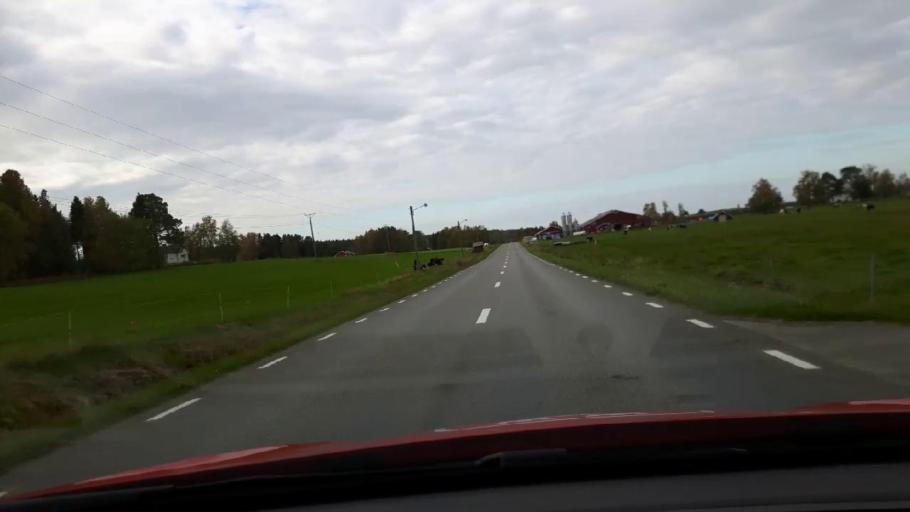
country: SE
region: Jaemtland
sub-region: Krokoms Kommun
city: Krokom
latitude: 63.1632
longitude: 14.1239
